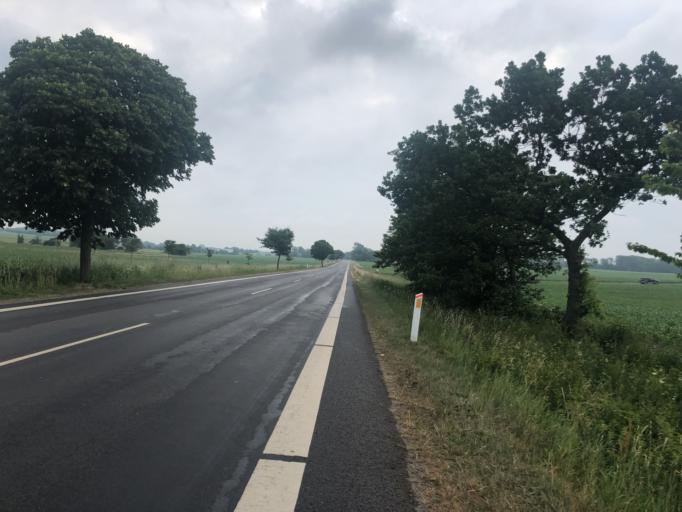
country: DK
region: Capital Region
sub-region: Bornholm Kommune
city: Akirkeby
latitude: 55.1520
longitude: 14.9059
